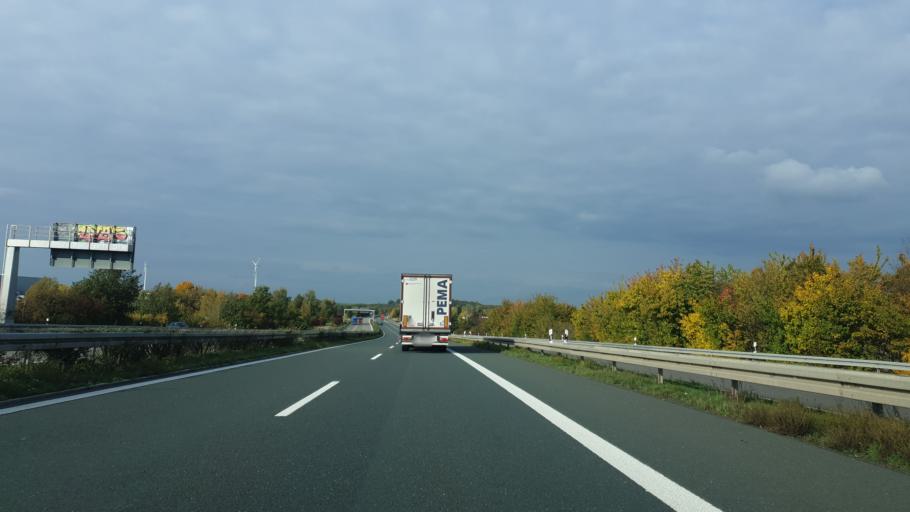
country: DE
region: Saxony
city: Dennheritz
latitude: 50.8264
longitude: 12.4487
